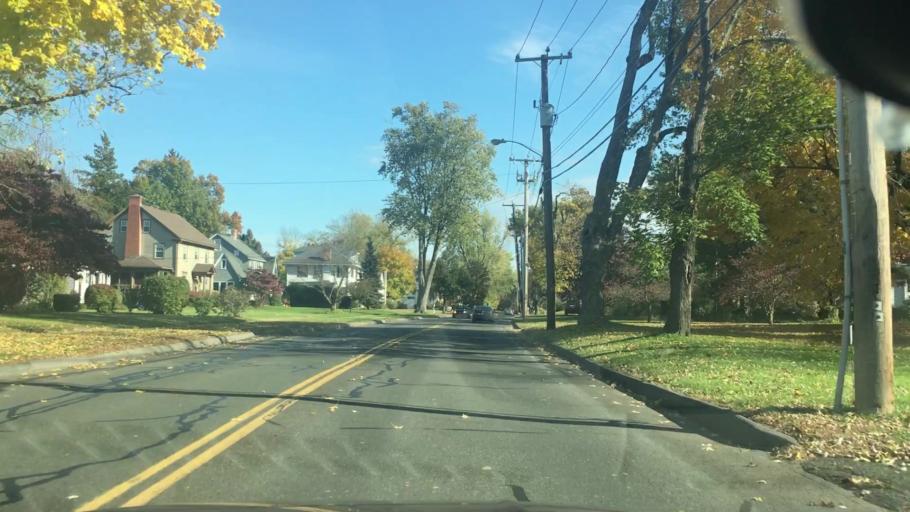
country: US
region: Massachusetts
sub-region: Hampden County
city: Longmeadow
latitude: 42.0327
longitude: -72.5810
